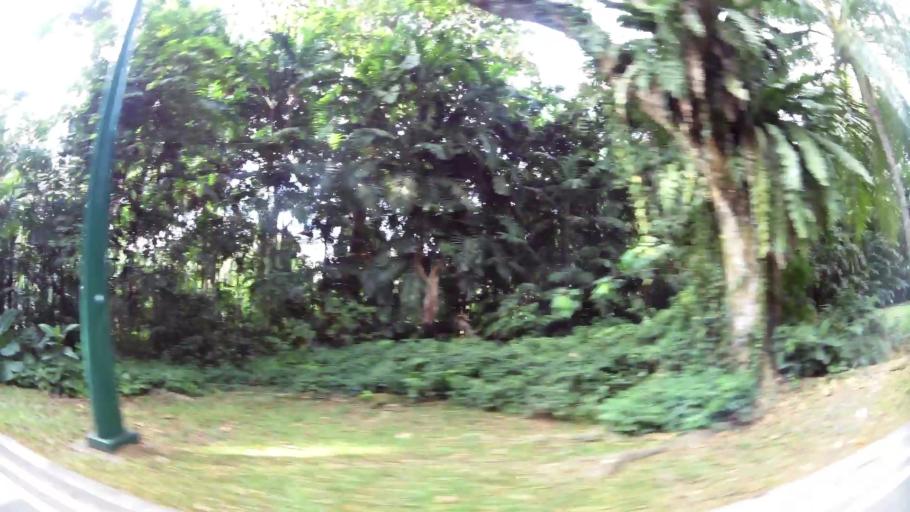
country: SG
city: Singapore
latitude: 1.2456
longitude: 103.8262
